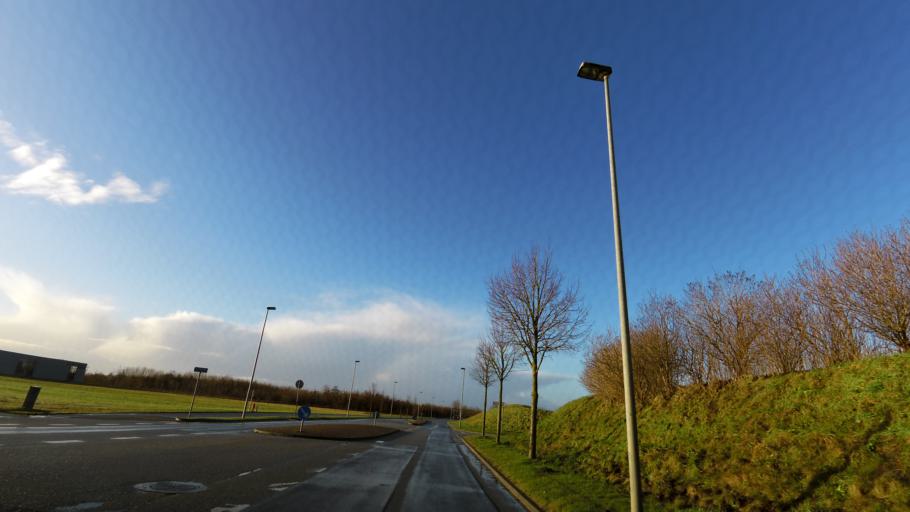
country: DK
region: Central Jutland
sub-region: Ikast-Brande Kommune
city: Ikast
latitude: 56.1211
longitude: 9.1653
